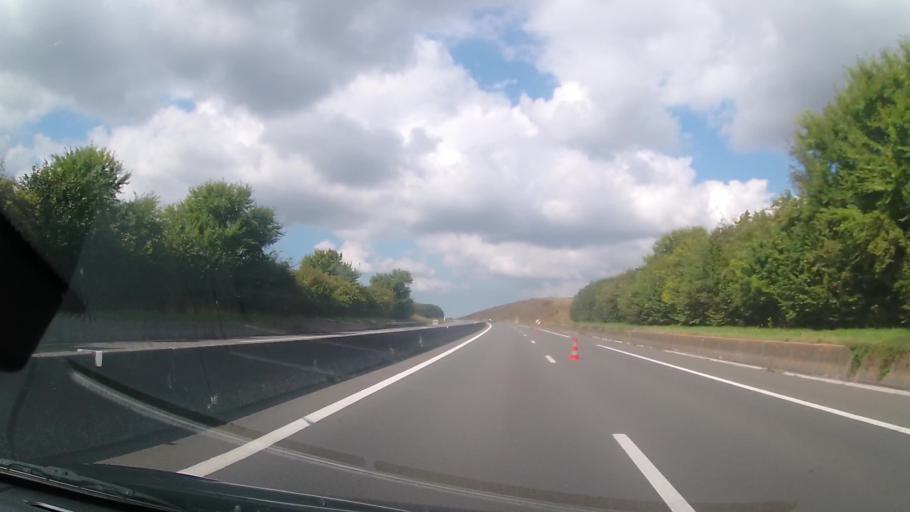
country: FR
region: Picardie
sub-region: Departement de la Somme
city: Rue
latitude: 50.3259
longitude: 1.7151
